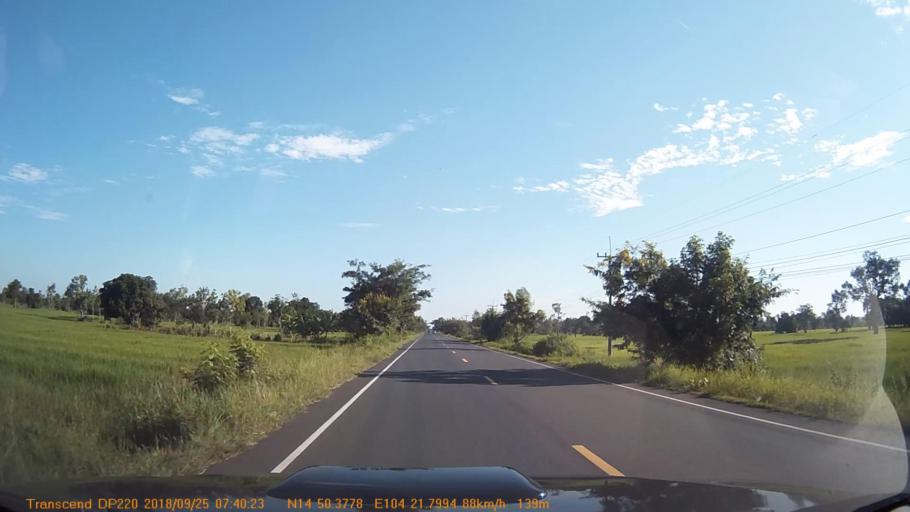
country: TH
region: Sisaket
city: Phayu
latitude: 14.8403
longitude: 104.3635
